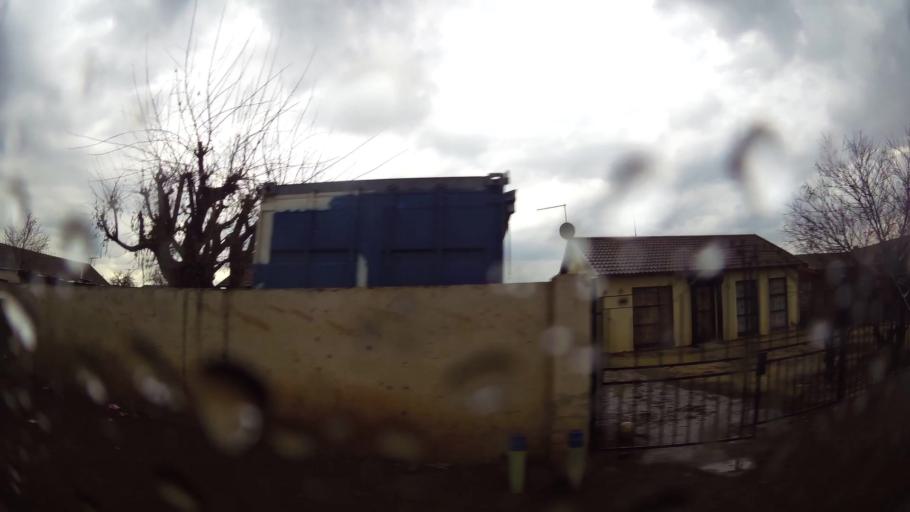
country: ZA
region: Gauteng
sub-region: Ekurhuleni Metropolitan Municipality
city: Germiston
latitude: -26.3638
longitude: 28.1341
